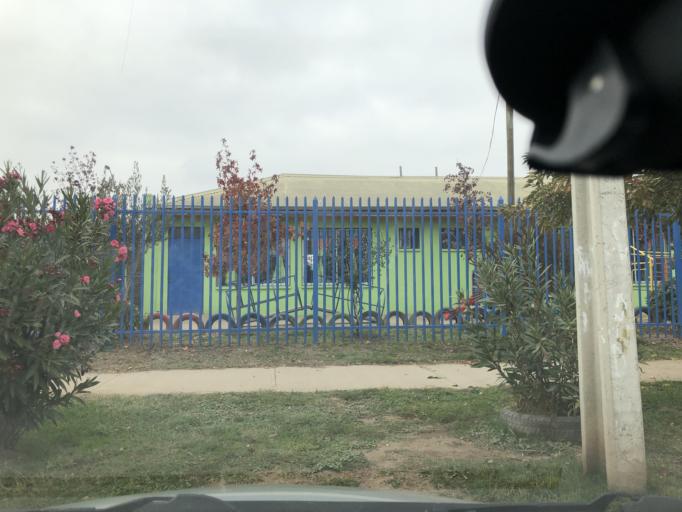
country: CL
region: Santiago Metropolitan
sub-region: Provincia de Santiago
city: La Pintana
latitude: -33.5695
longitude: -70.6068
